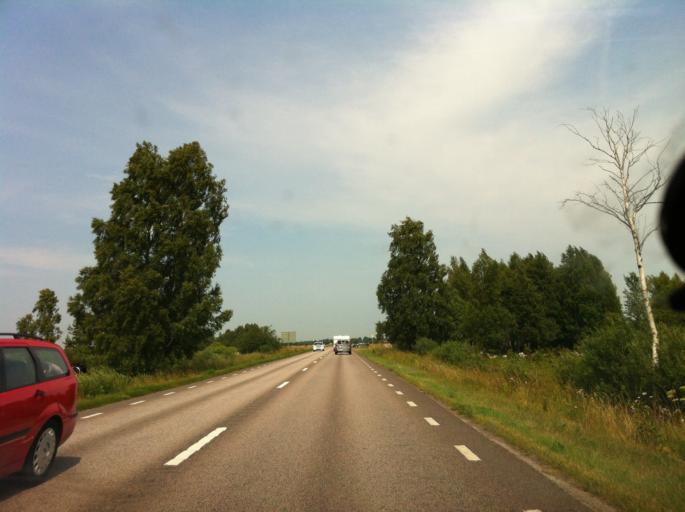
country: SE
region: Kalmar
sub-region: Borgholms Kommun
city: Borgholm
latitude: 56.9308
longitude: 16.7679
